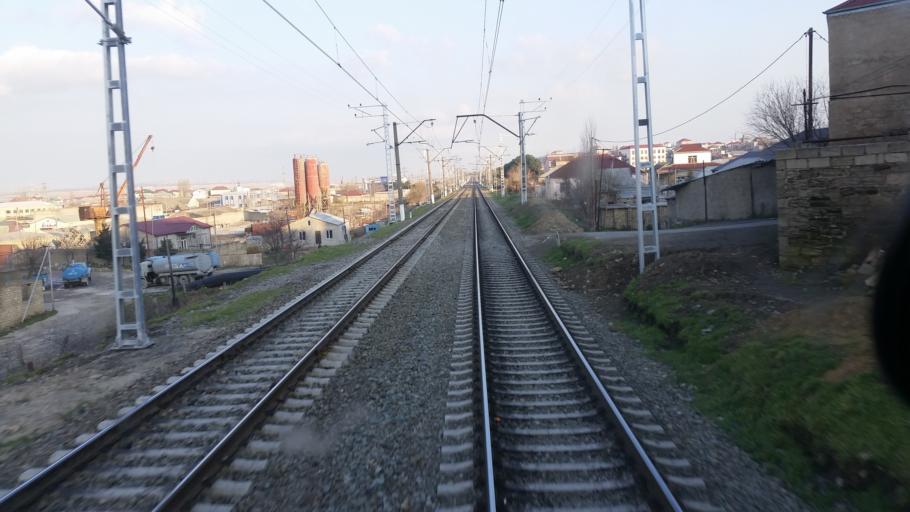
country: AZ
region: Baki
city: Binagadi
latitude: 40.4399
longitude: 49.8392
